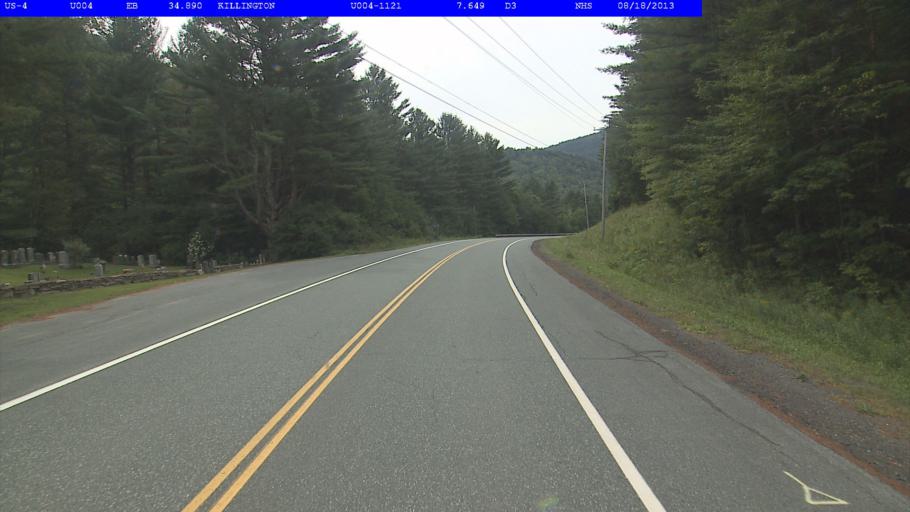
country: US
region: Vermont
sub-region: Rutland County
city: Rutland
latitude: 43.6122
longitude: -72.7528
